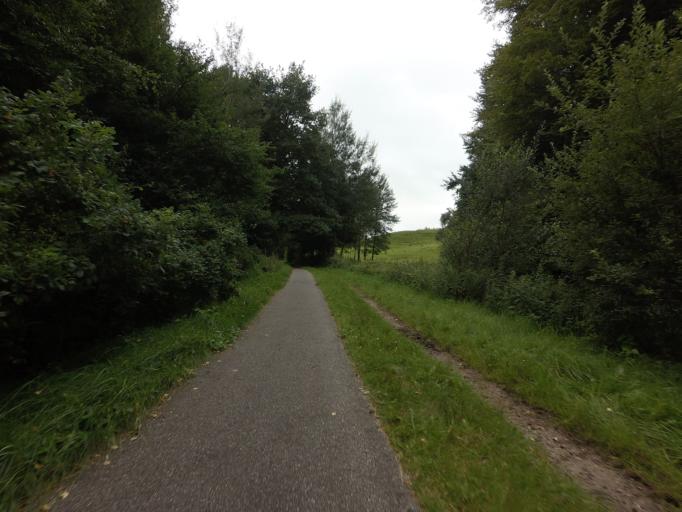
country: DK
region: Central Jutland
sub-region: Silkeborg Kommune
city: Virklund
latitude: 56.1075
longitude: 9.5595
